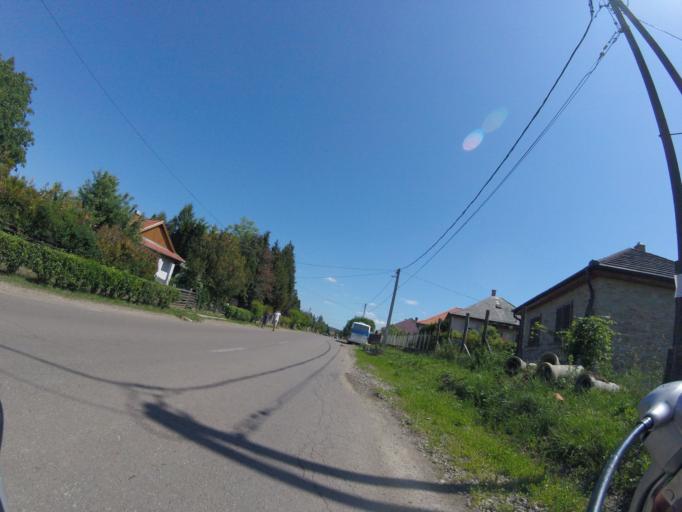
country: HU
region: Heves
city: Recsk
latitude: 47.9277
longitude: 20.0942
